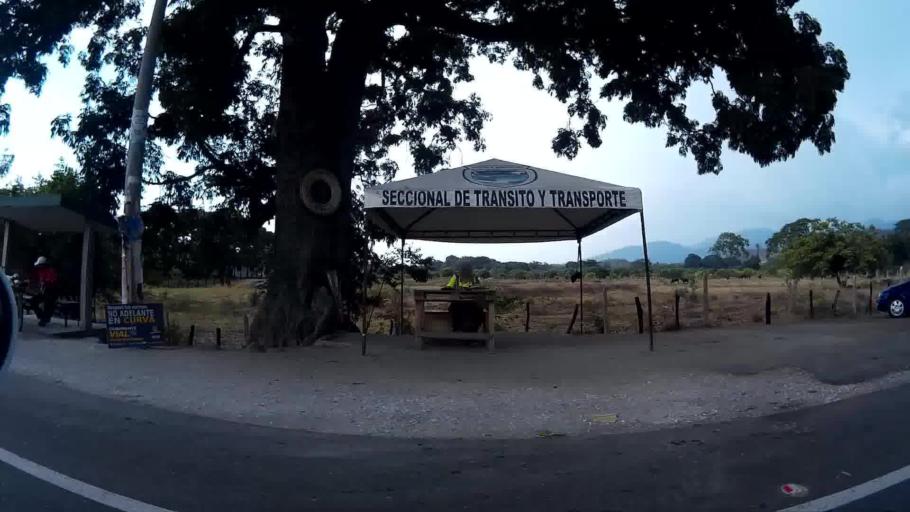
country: CO
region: Magdalena
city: Cienaga
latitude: 11.0038
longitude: -74.2204
